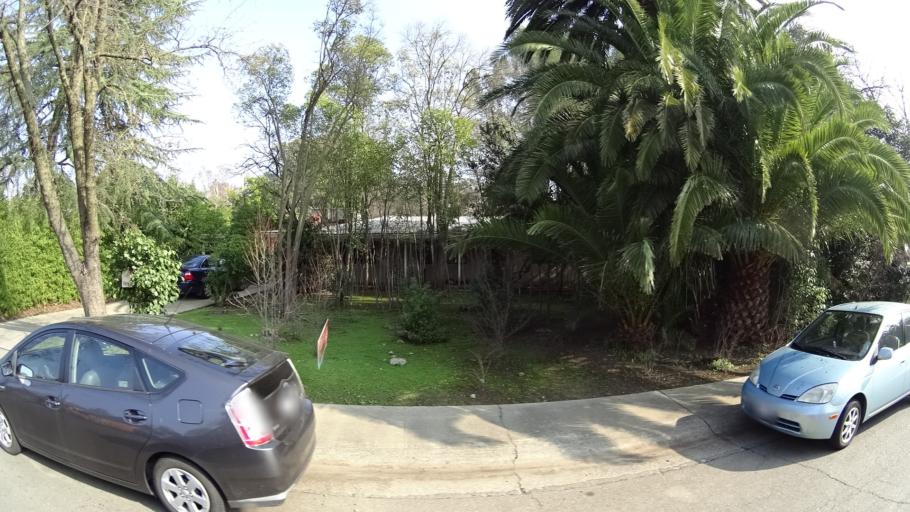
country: US
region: California
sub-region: Yolo County
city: Davis
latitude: 38.5602
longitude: -121.7536
